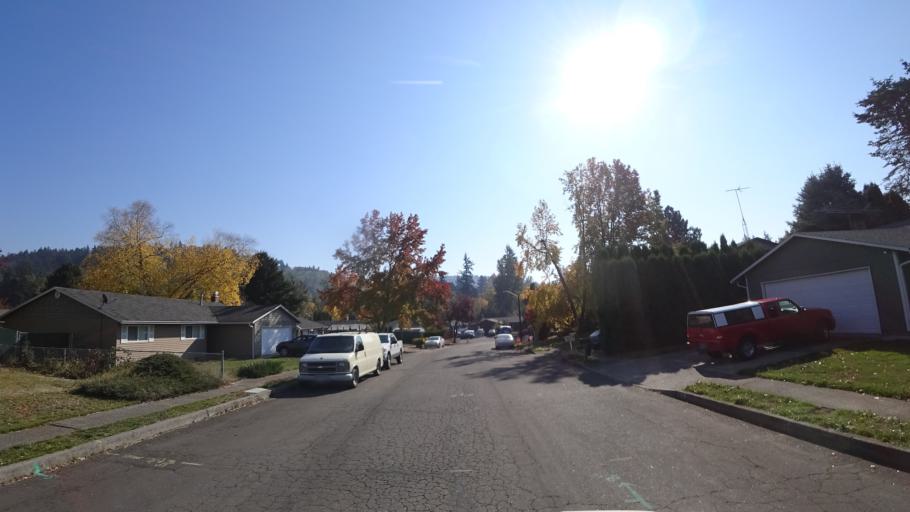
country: US
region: Oregon
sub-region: Multnomah County
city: Gresham
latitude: 45.4906
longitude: -122.4515
